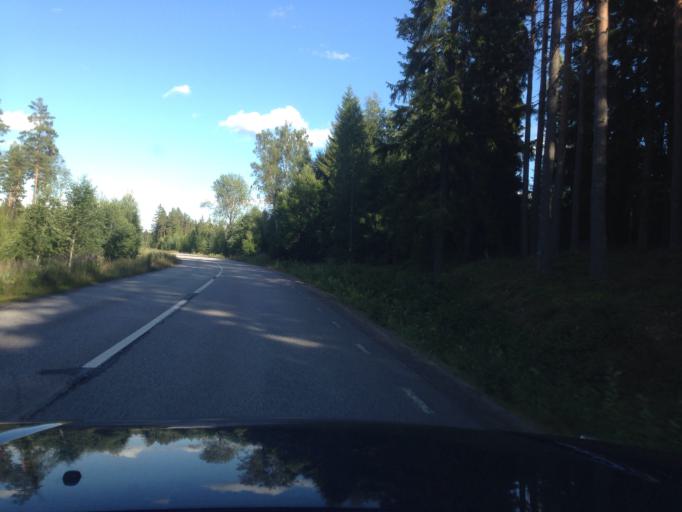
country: SE
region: Dalarna
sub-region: Ludvika Kommun
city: Abborrberget
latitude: 60.2076
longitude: 14.8943
